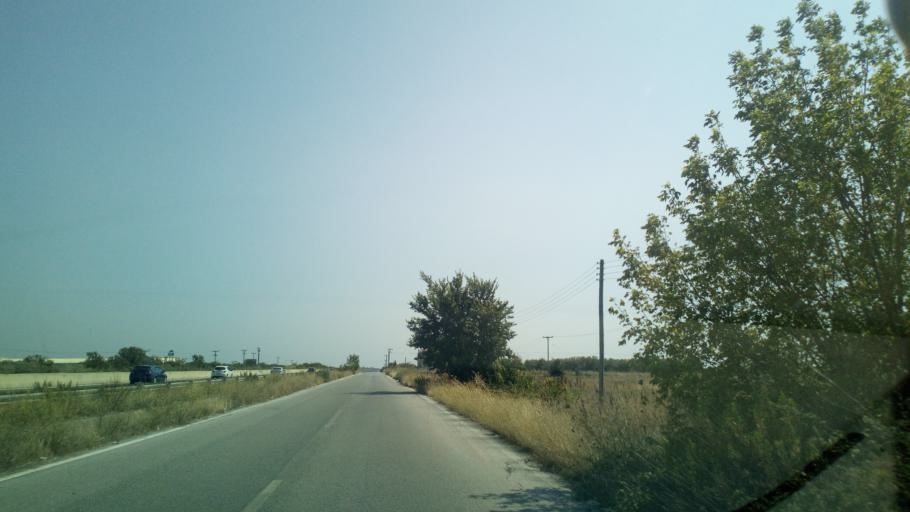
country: GR
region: Central Macedonia
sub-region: Nomos Chalkidikis
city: Lakkoma
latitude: 40.3793
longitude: 23.0407
